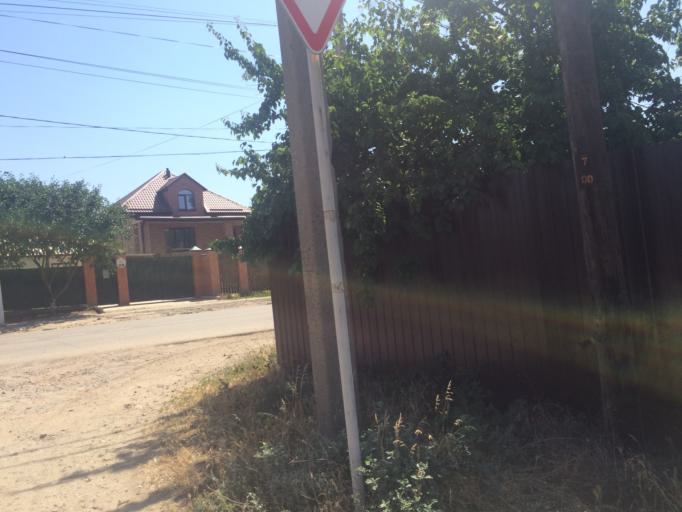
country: RU
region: Rostov
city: Sal'sk
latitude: 46.4765
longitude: 41.5459
